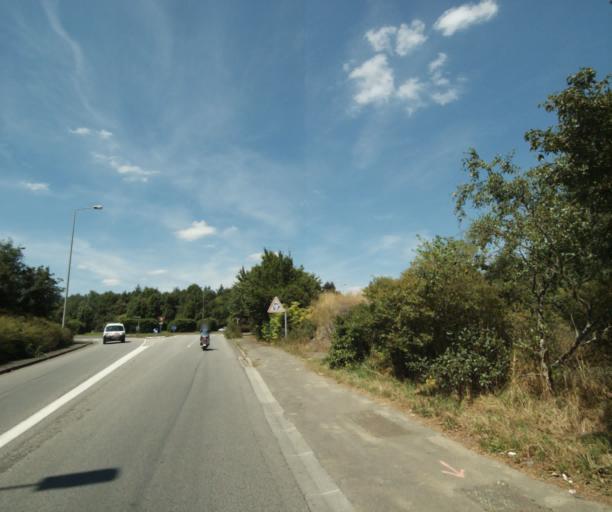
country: FR
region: Pays de la Loire
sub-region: Departement de la Mayenne
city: Change
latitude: 48.0896
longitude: -0.7745
